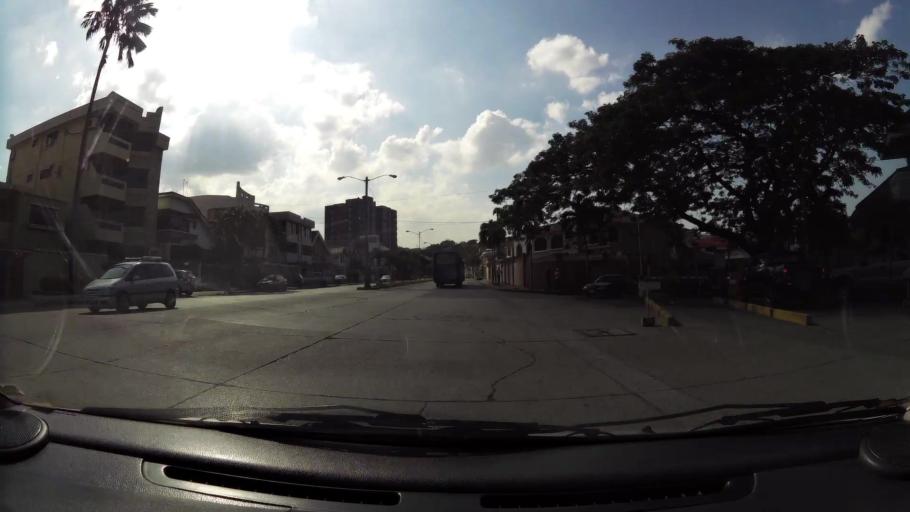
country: EC
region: Guayas
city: Santa Lucia
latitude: -2.1610
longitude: -79.9469
